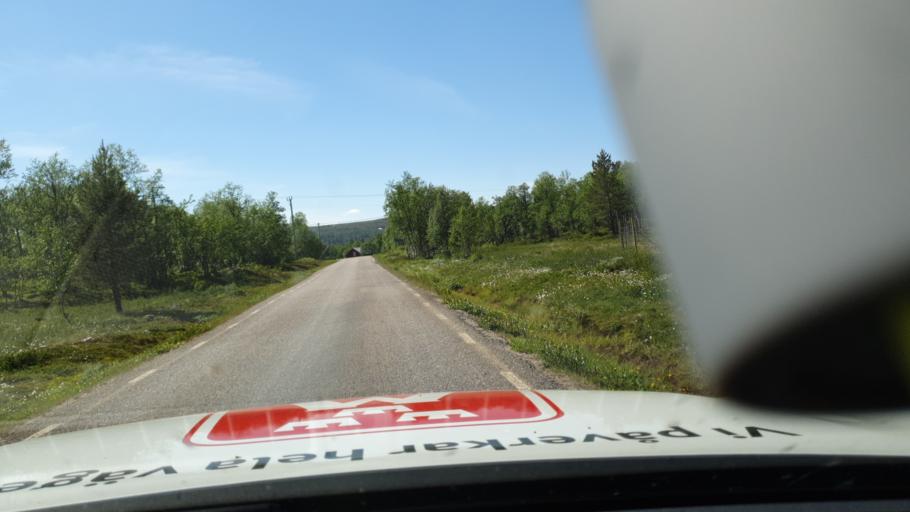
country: NO
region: Hedmark
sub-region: Engerdal
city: Engerdal
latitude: 62.1493
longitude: 12.9710
